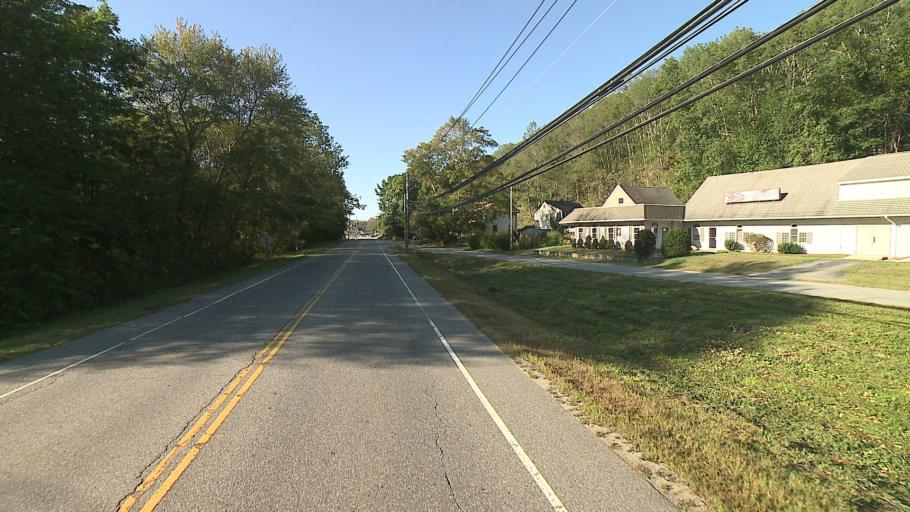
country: US
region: Connecticut
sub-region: Windham County
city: Moosup
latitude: 41.7141
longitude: -71.9038
